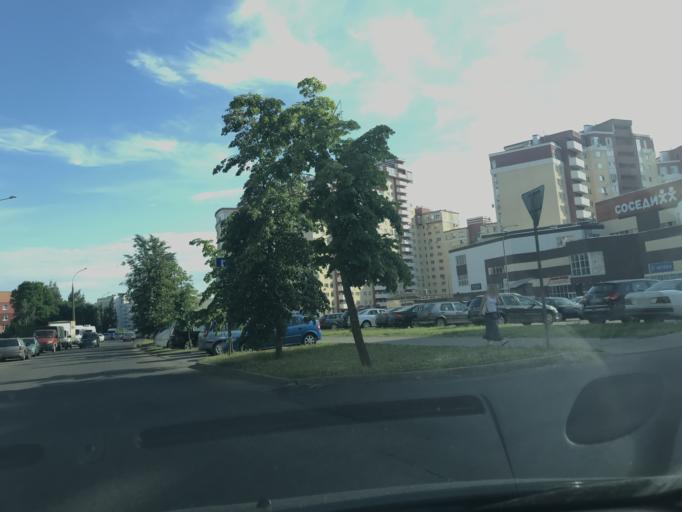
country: BY
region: Minsk
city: Borovlyany
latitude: 53.9503
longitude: 27.6836
